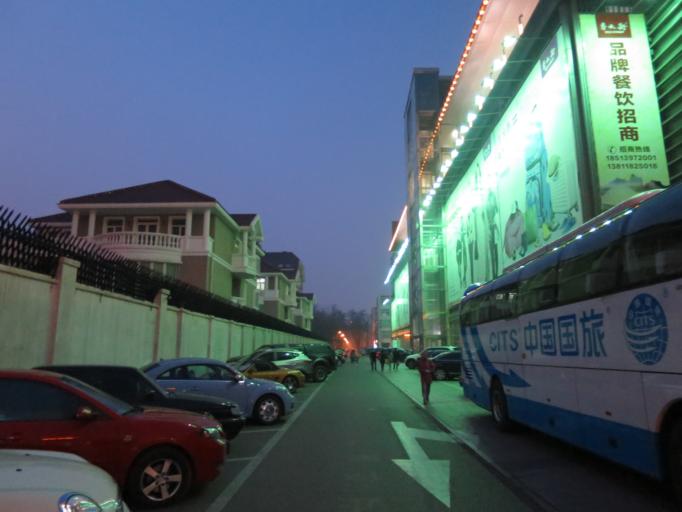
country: CN
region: Beijing
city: Chaowai
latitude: 39.9082
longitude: 116.4431
